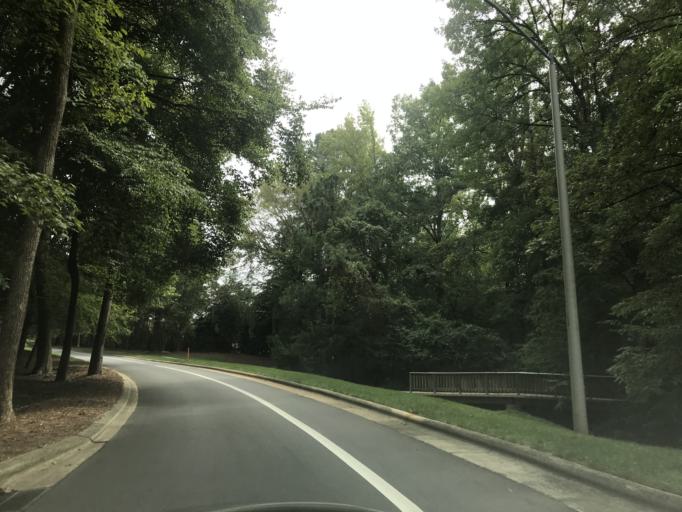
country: US
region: North Carolina
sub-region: Wake County
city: Cary
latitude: 35.7337
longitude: -78.7856
